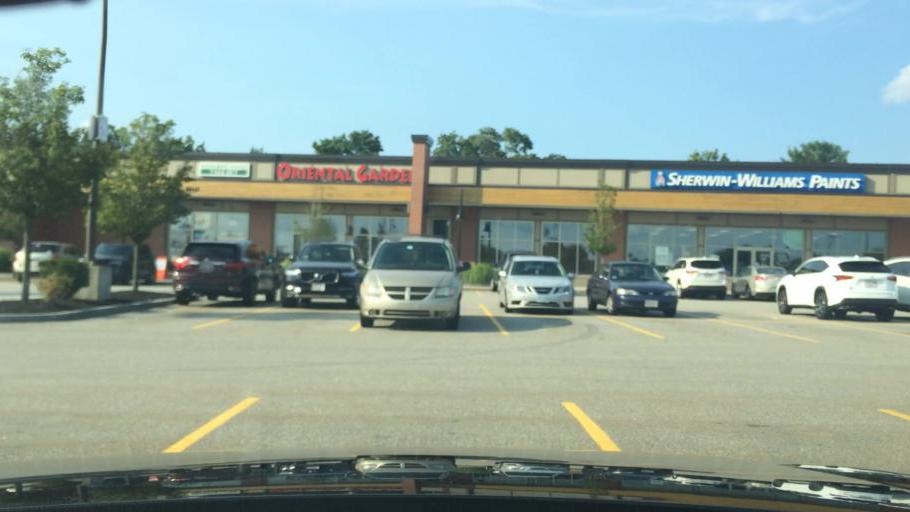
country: US
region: Massachusetts
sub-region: Essex County
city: Haverhill
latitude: 42.7745
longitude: -71.1149
